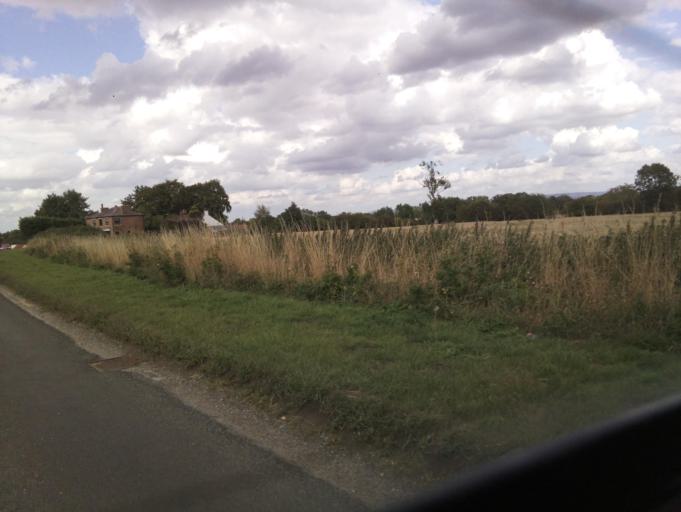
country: GB
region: England
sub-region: North Yorkshire
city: Ripon
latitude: 54.1579
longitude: -1.5413
